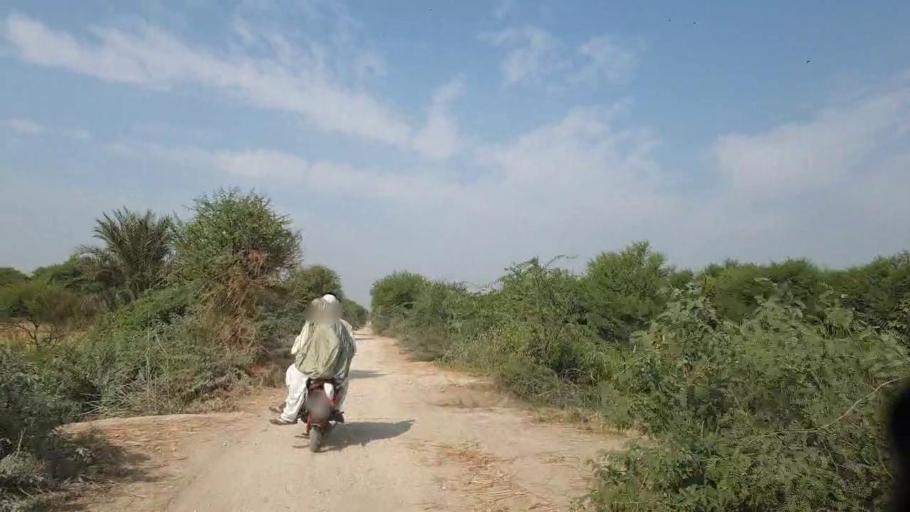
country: PK
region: Sindh
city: Tando Muhammad Khan
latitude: 25.0594
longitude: 68.4182
